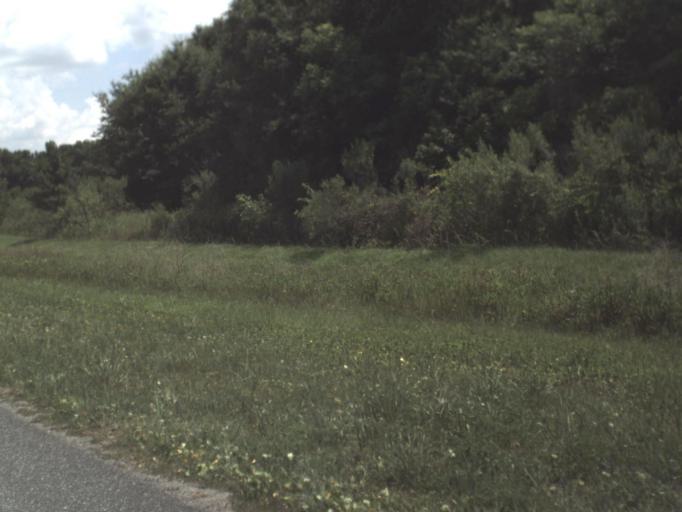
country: US
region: Florida
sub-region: Bradford County
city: Starke
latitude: 30.0206
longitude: -82.0506
